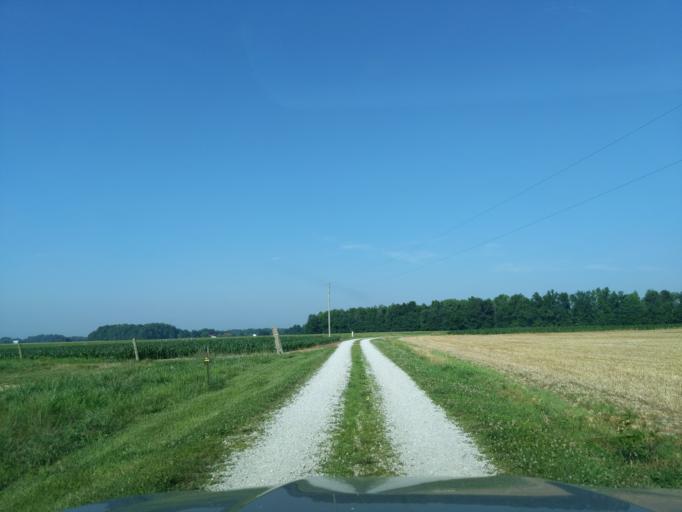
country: US
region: Indiana
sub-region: Decatur County
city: Greensburg
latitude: 39.2166
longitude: -85.4152
